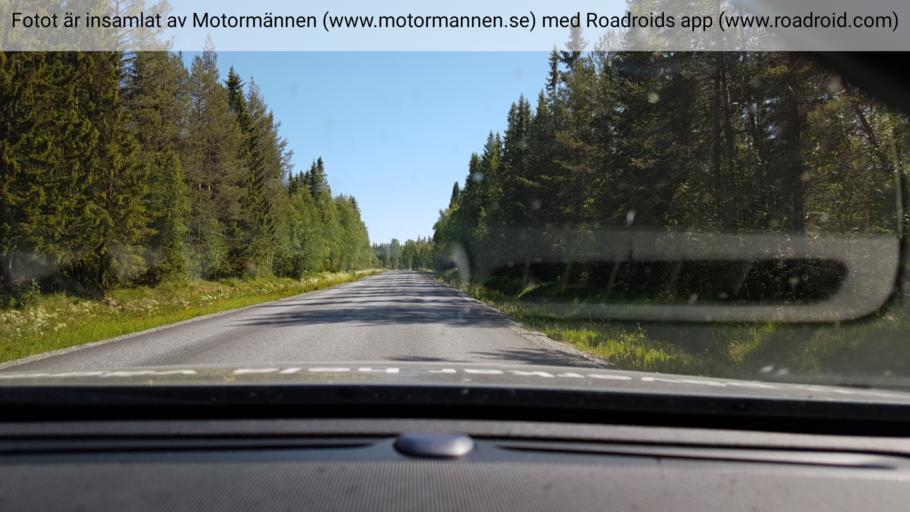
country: SE
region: Vaesterbotten
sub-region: Vilhelmina Kommun
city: Sjoberg
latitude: 64.7240
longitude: 16.2290
